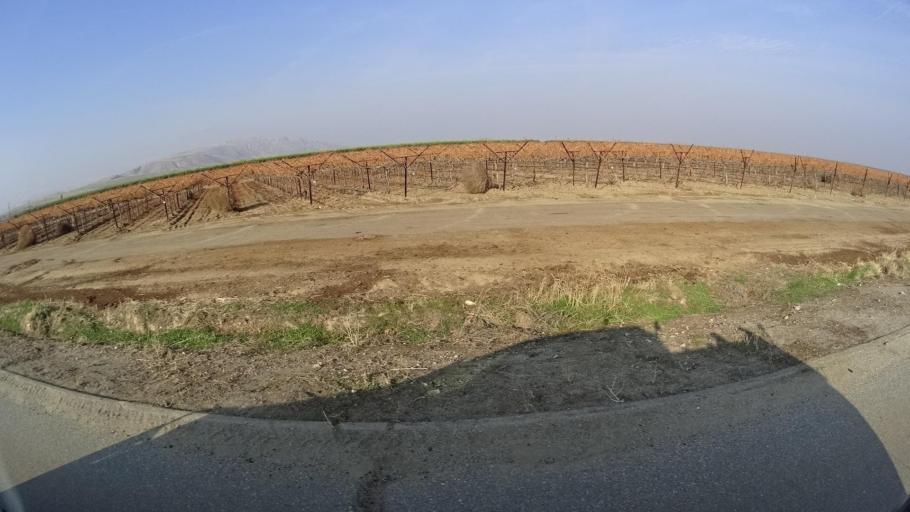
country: US
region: California
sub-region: Kern County
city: Lebec
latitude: 35.0086
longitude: -118.9411
